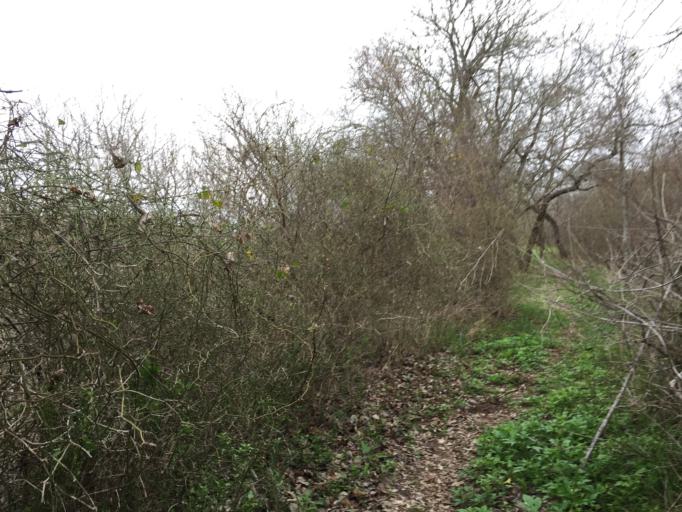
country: US
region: Texas
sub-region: Bastrop County
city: Bastrop
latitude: 30.0820
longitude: -97.3259
